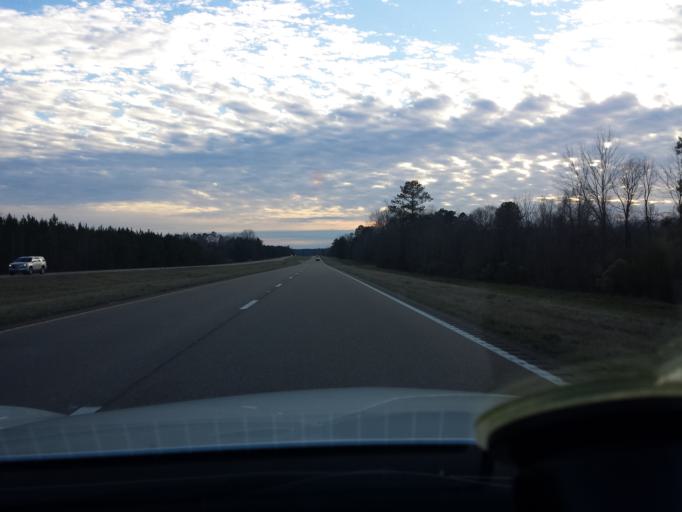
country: US
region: Mississippi
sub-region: Oktibbeha County
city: Starkville
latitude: 33.3975
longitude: -88.8599
